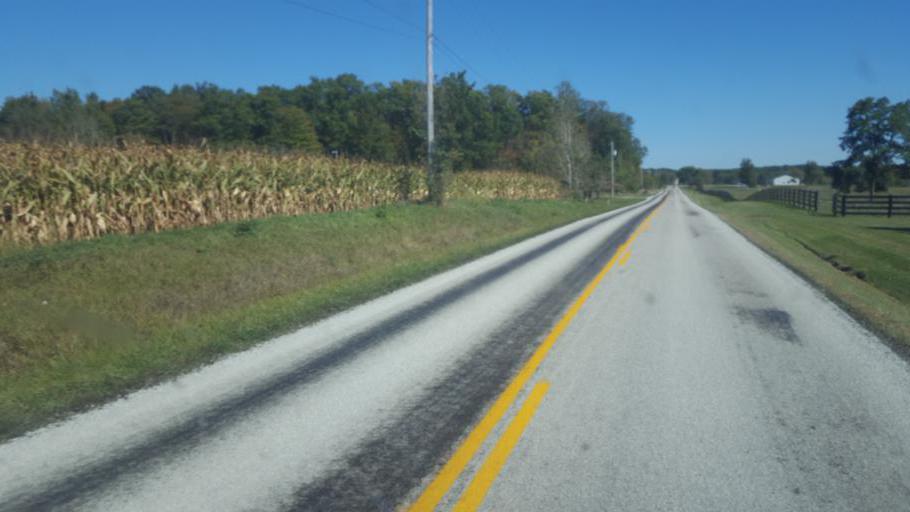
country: US
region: Ohio
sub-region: Ashland County
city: Ashland
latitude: 40.9928
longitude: -82.2661
